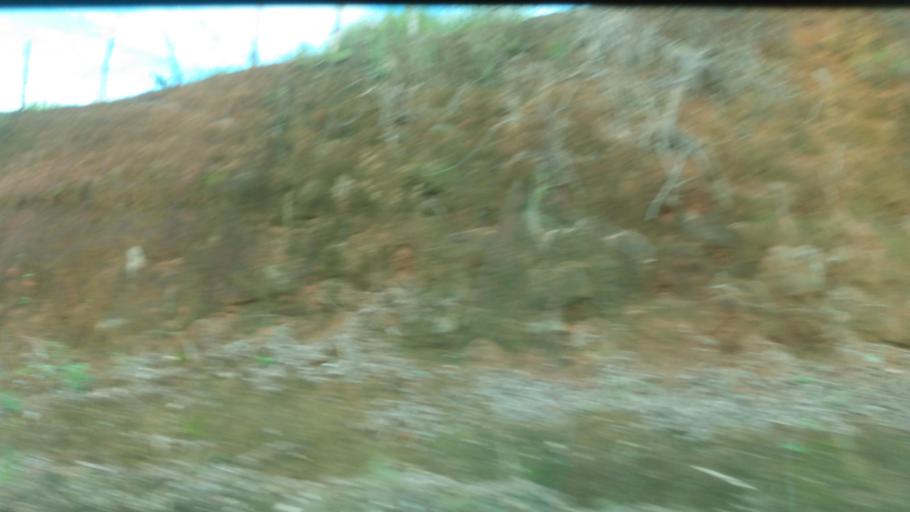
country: BR
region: Pernambuco
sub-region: Catende
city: Catende
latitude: -8.7047
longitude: -35.7586
